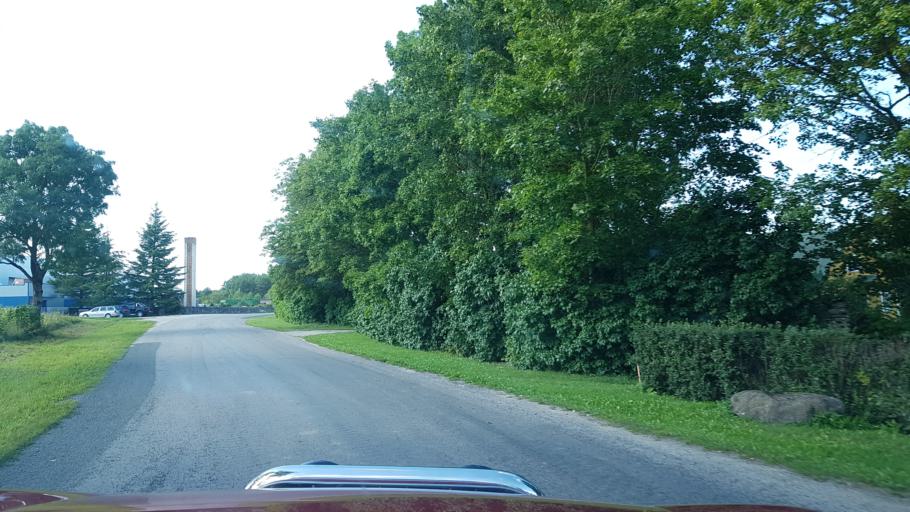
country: EE
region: Harju
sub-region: Paldiski linn
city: Paldiski
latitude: 59.2362
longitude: 24.0202
